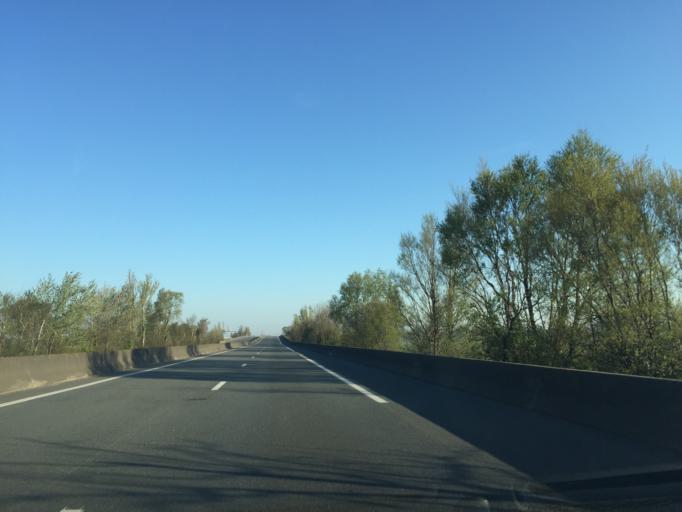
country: FR
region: Nord-Pas-de-Calais
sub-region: Departement du Nord
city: Loon-Plage
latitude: 50.9839
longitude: 2.2098
